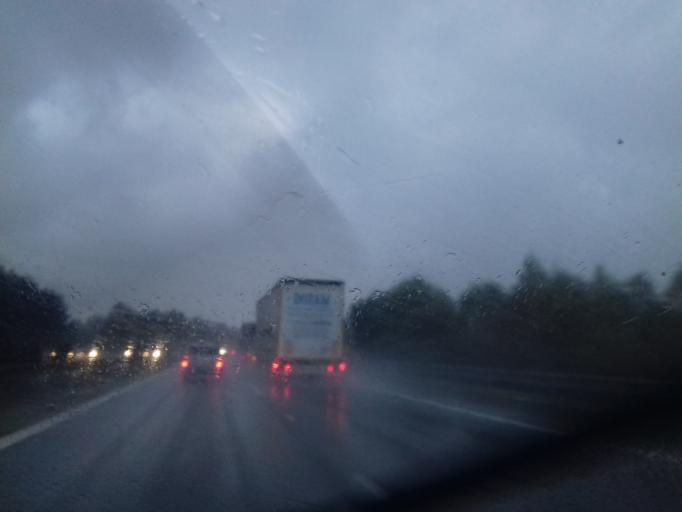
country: CZ
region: Vysocina
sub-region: Okres Pelhrimov
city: Humpolec
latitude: 49.5291
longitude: 15.3415
